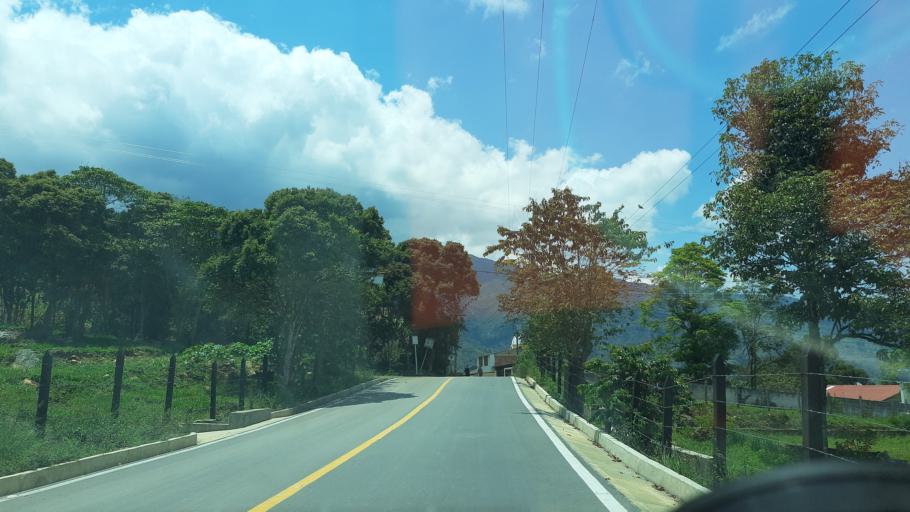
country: CO
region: Boyaca
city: Chinavita
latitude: 5.1374
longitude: -73.3950
